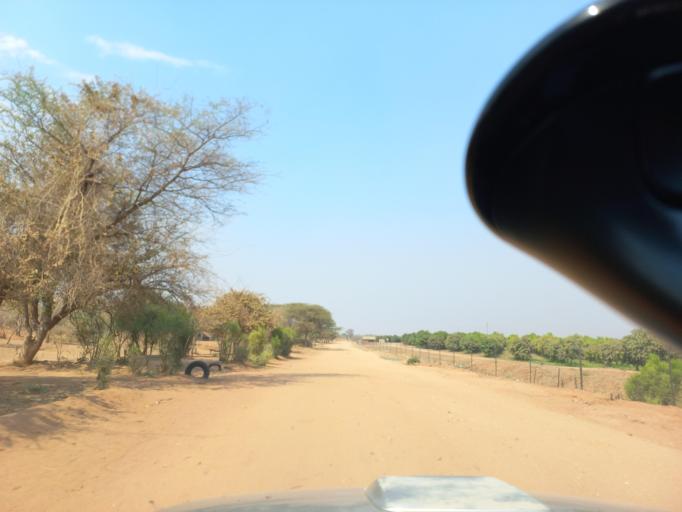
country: ZW
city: Chirundu
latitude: -15.9327
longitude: 28.9482
